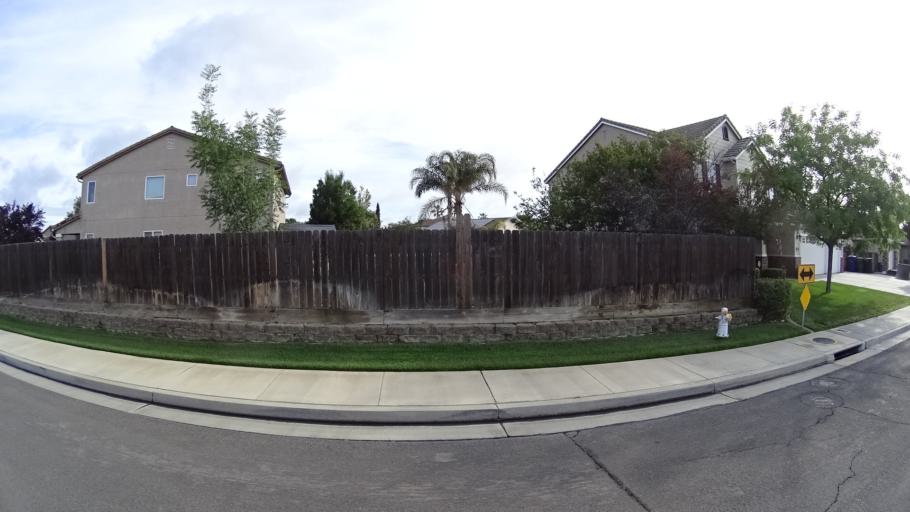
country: US
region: California
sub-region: Kings County
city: Lucerne
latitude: 36.3486
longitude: -119.6779
